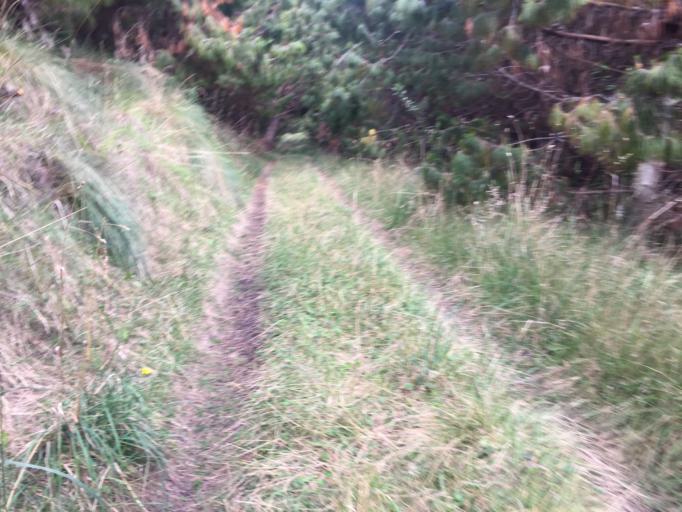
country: EC
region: Imbabura
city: Ibarra
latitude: 0.2249
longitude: -78.1269
